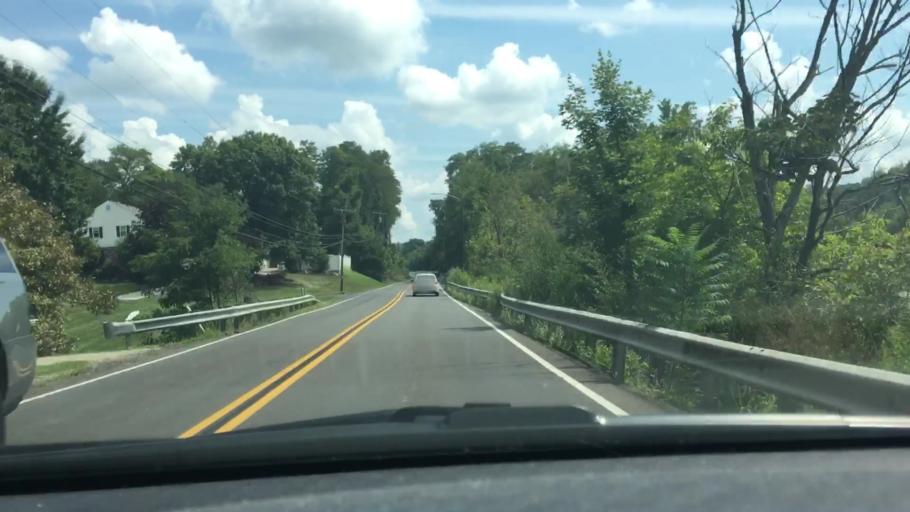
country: US
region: Pennsylvania
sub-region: Washington County
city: Thompsonville
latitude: 40.2542
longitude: -80.1258
